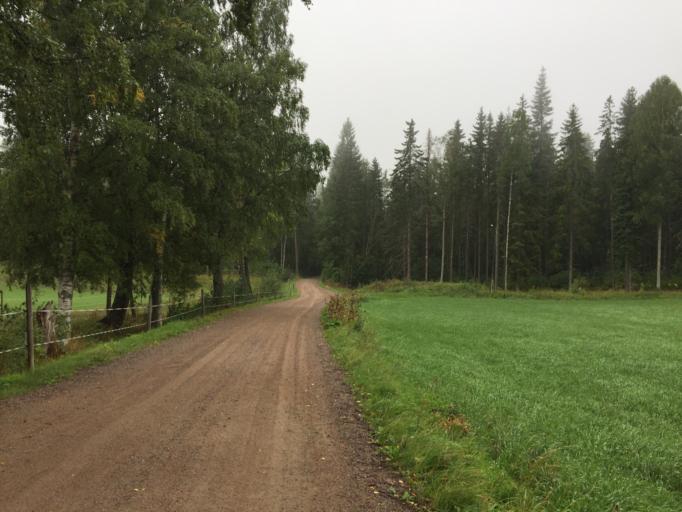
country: NO
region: Akershus
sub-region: Baerum
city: Lysaker
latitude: 59.9764
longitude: 10.6348
